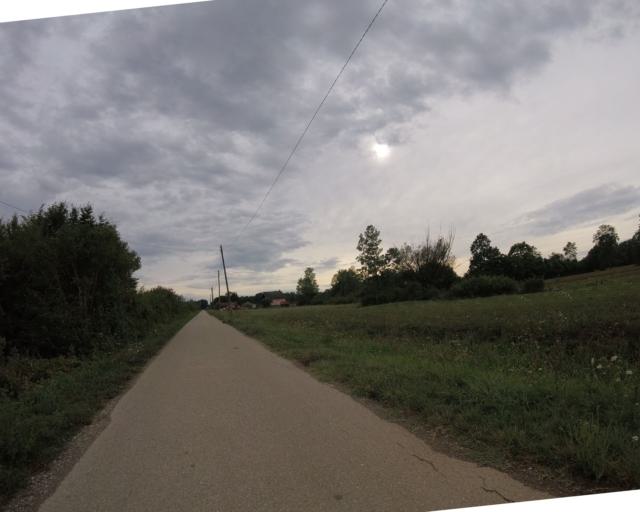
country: HR
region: Zagrebacka
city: Kuce
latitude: 45.7150
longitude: 16.1724
